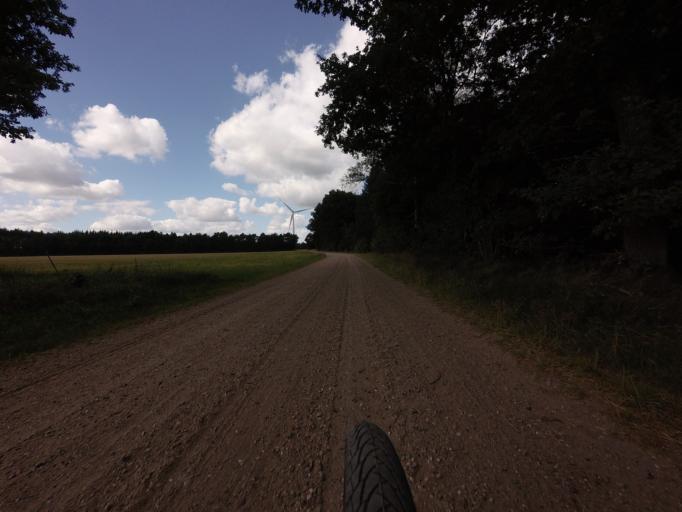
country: DK
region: Central Jutland
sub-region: Ikast-Brande Kommune
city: Brande
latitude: 55.9732
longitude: 9.1398
